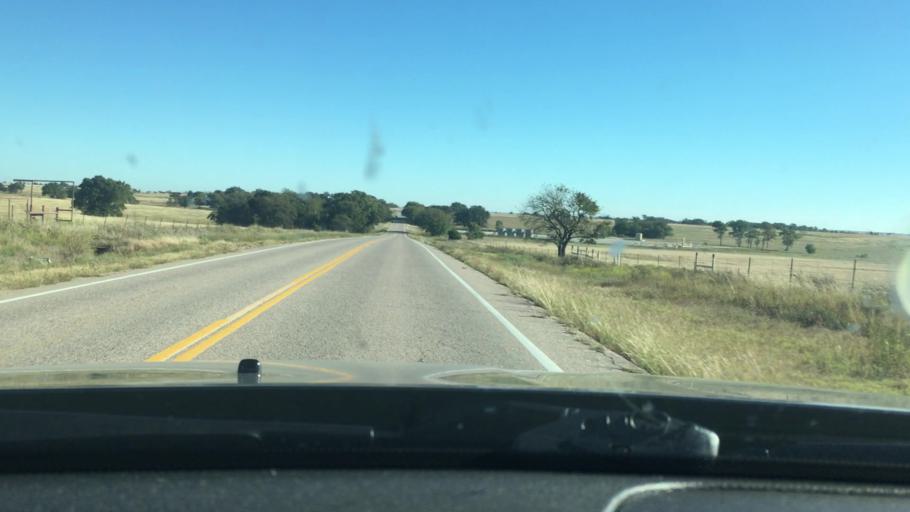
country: US
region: Oklahoma
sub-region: Marshall County
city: Madill
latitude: 34.1232
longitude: -96.7290
